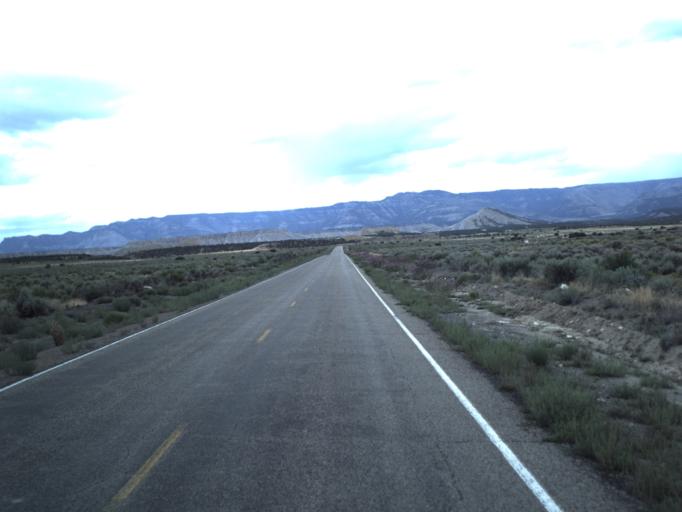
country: US
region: Utah
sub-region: Carbon County
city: Price
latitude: 39.4875
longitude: -110.8732
